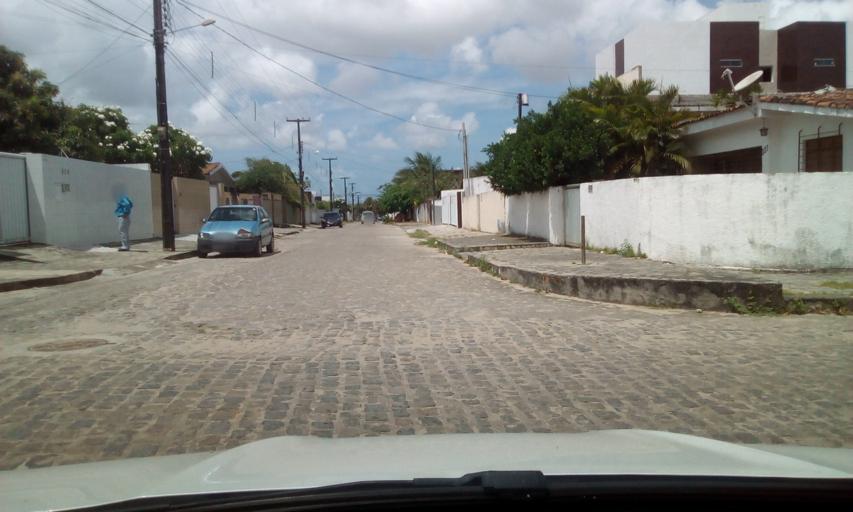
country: BR
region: Paraiba
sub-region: Bayeux
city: Bayeux
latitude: -7.1776
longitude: -34.9165
